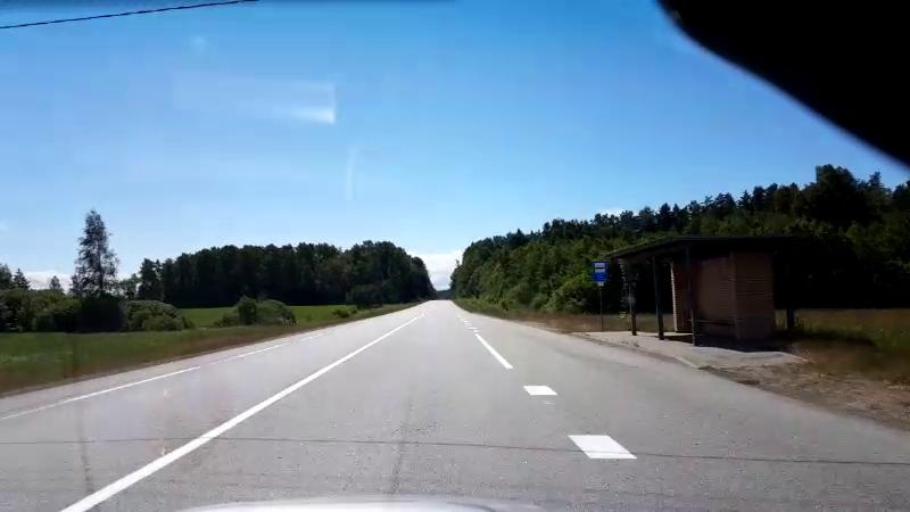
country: LV
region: Saulkrastu
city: Saulkrasti
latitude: 57.4330
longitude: 24.4298
